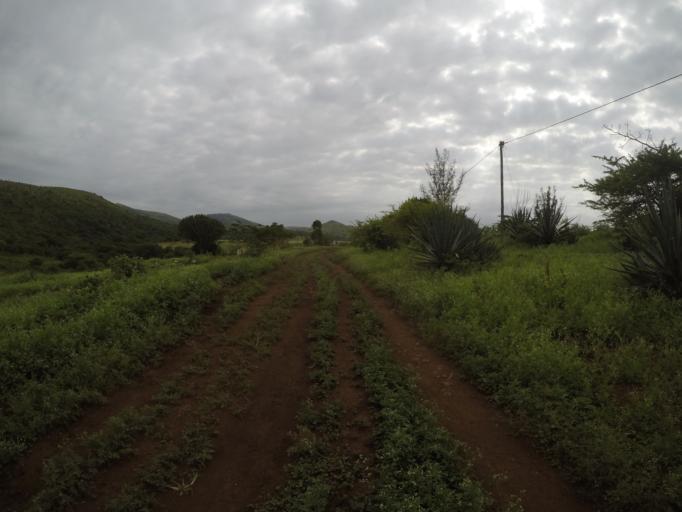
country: ZA
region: KwaZulu-Natal
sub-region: uThungulu District Municipality
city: Empangeni
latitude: -28.6398
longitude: 31.9092
